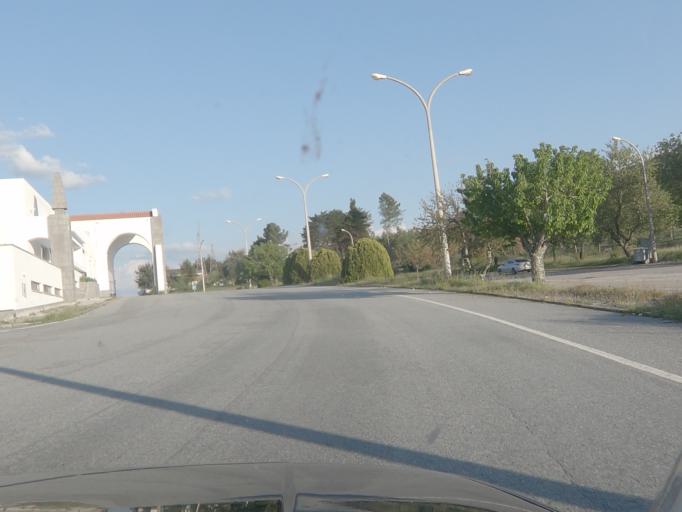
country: PT
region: Portalegre
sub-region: Portalegre
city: Sao Juliao
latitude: 39.3524
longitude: -7.3082
